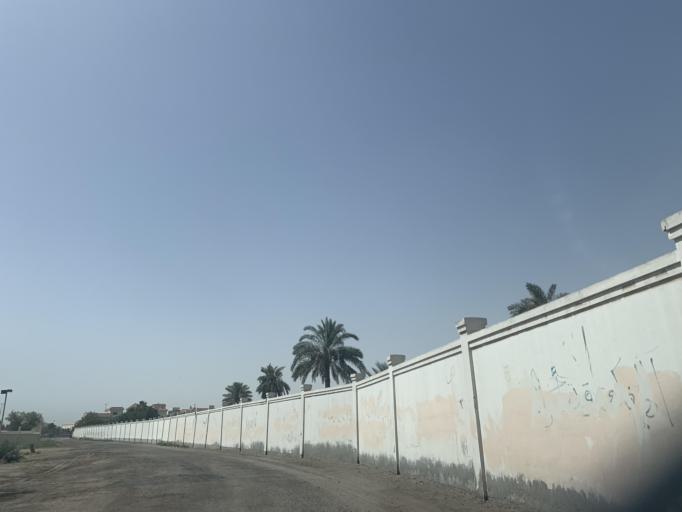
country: BH
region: Manama
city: Jidd Hafs
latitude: 26.2024
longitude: 50.5561
